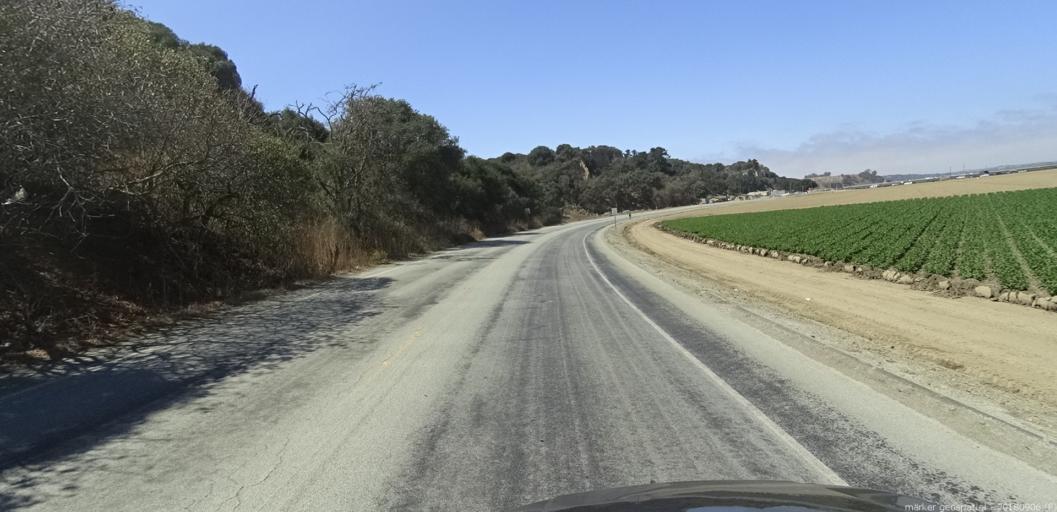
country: US
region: California
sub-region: Monterey County
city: Salinas
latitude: 36.6422
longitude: -121.7123
